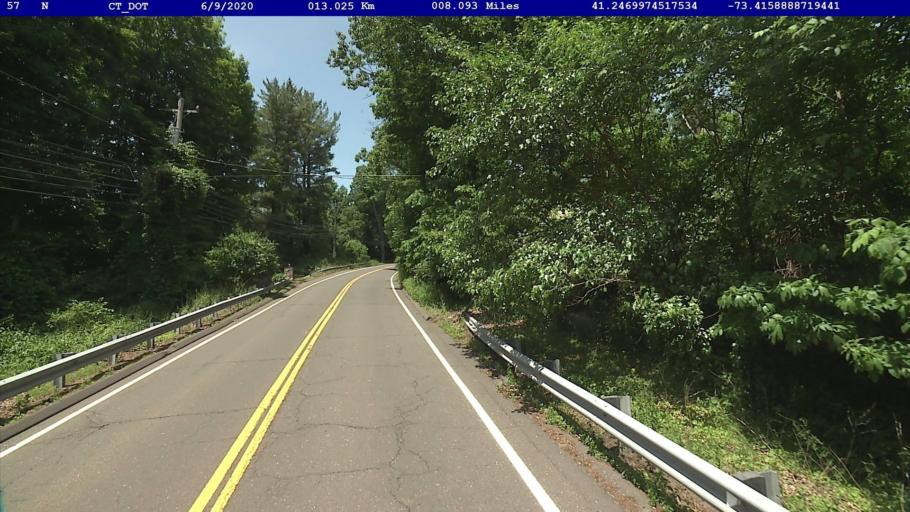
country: US
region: Connecticut
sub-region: Fairfield County
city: Georgetown
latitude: 41.2470
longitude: -73.4159
